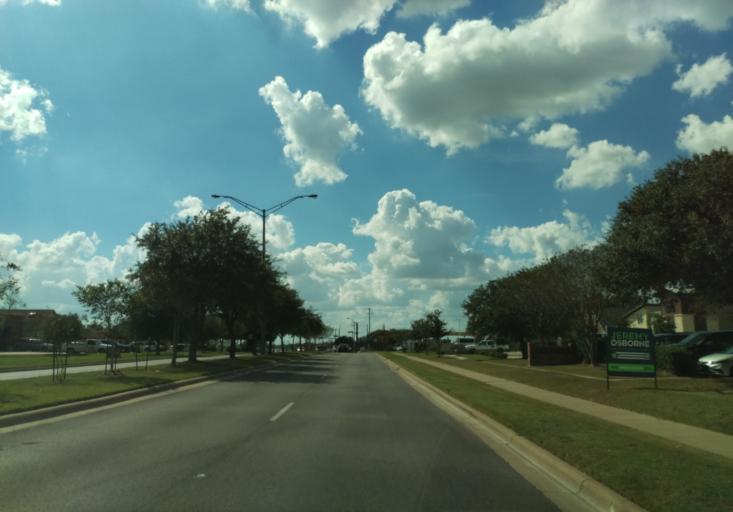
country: US
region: Texas
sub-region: Brazos County
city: College Station
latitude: 30.5725
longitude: -96.3091
